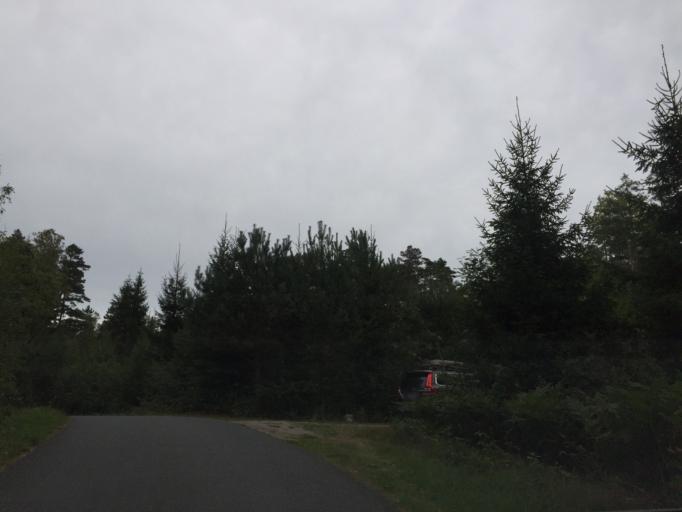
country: NO
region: Ostfold
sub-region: Hvaler
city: Skjaerhalden
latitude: 59.0783
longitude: 11.0055
